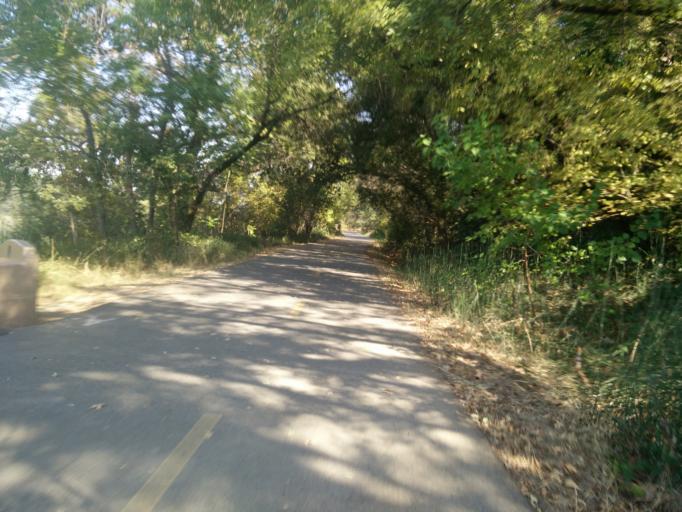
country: US
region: California
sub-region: Shasta County
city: Redding
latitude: 40.5920
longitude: -122.4114
